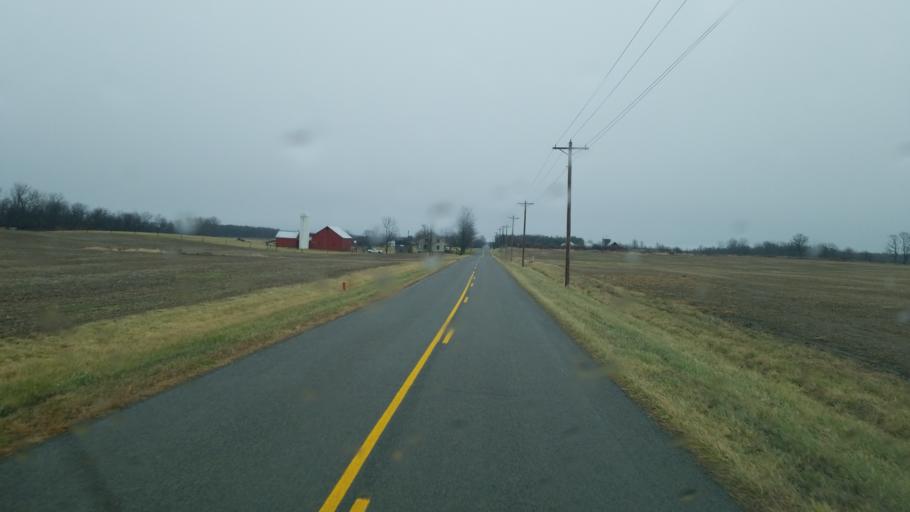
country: US
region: Ohio
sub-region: Logan County
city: Northwood
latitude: 40.4469
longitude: -83.6246
